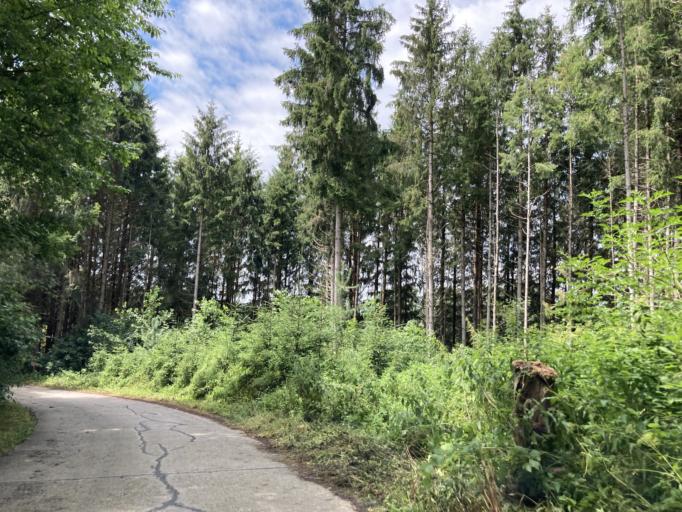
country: DE
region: Bavaria
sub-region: Upper Bavaria
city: Vogtareuth
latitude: 47.9465
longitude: 12.1704
